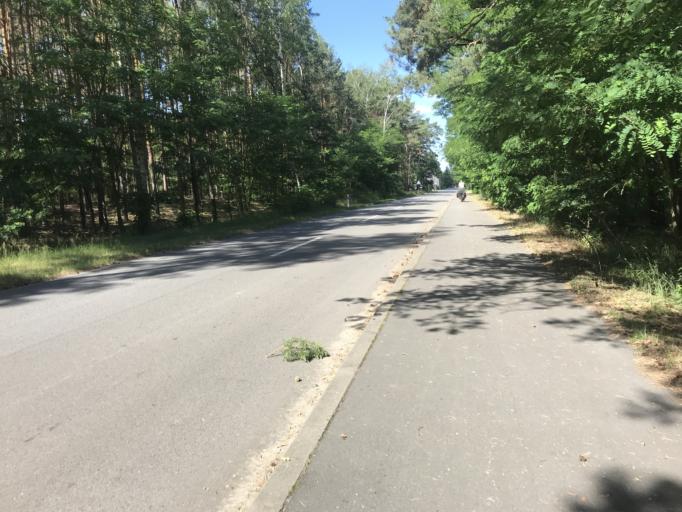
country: PL
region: Lubusz
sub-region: Powiat krosnienski
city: Gubin
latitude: 52.0604
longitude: 14.7694
